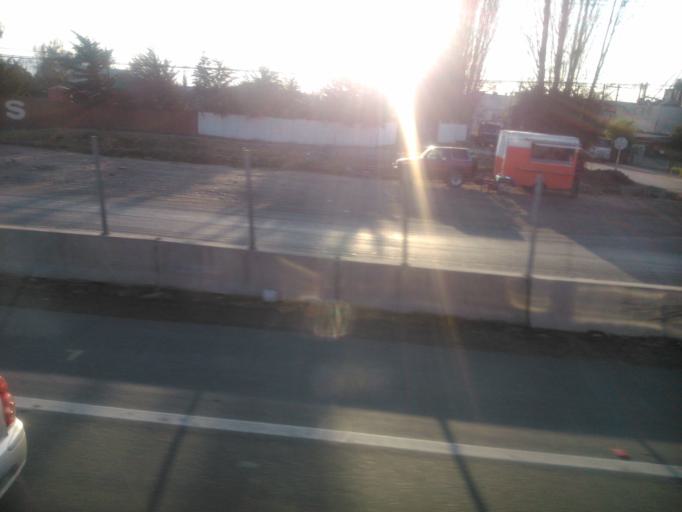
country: CL
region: Santiago Metropolitan
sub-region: Provincia de Maipo
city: Paine
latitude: -33.7784
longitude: -70.7445
